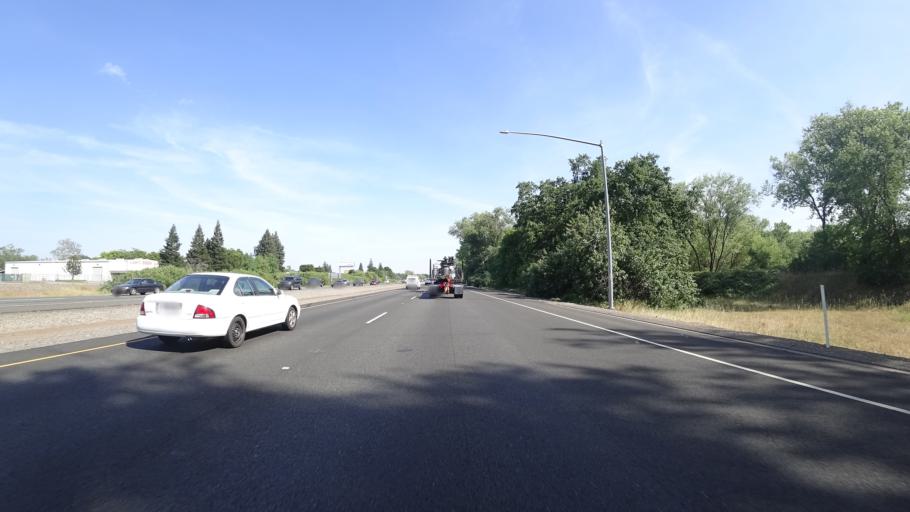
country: US
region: California
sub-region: Butte County
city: Durham
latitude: 39.6999
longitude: -121.7846
